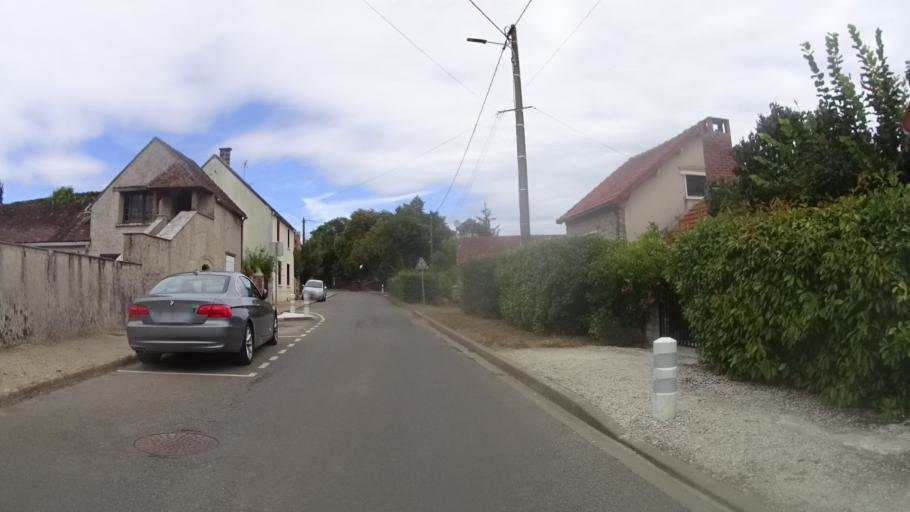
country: FR
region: Centre
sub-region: Departement du Loiret
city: Malesherbes
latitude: 48.2342
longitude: 2.4294
